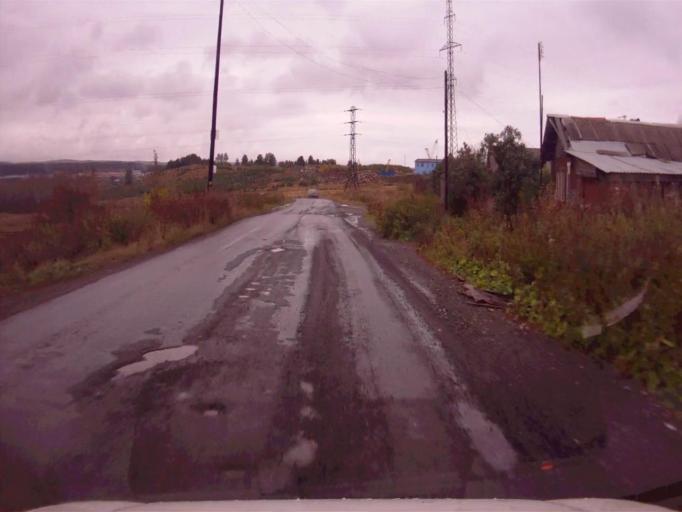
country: RU
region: Chelyabinsk
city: Verkhniy Ufaley
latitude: 56.0603
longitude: 60.1996
